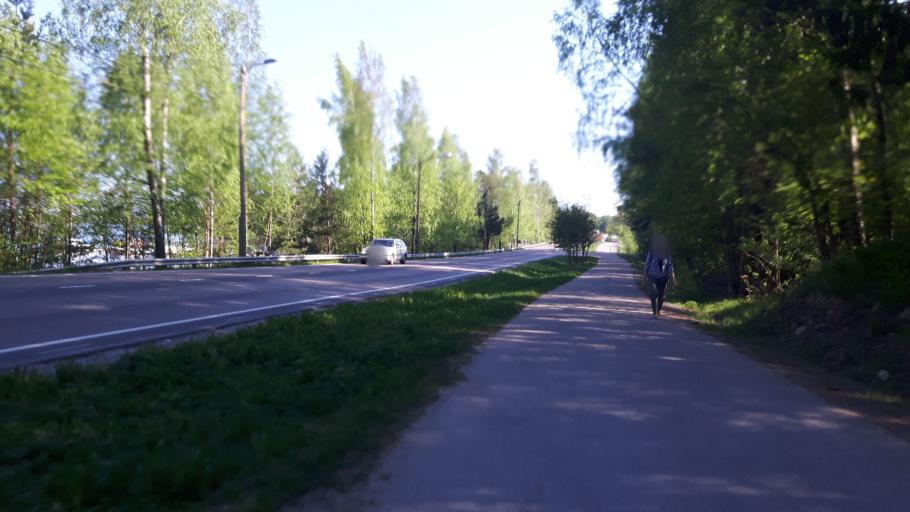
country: FI
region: Kymenlaakso
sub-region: Kotka-Hamina
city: Kotka
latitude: 60.4737
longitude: 26.8772
